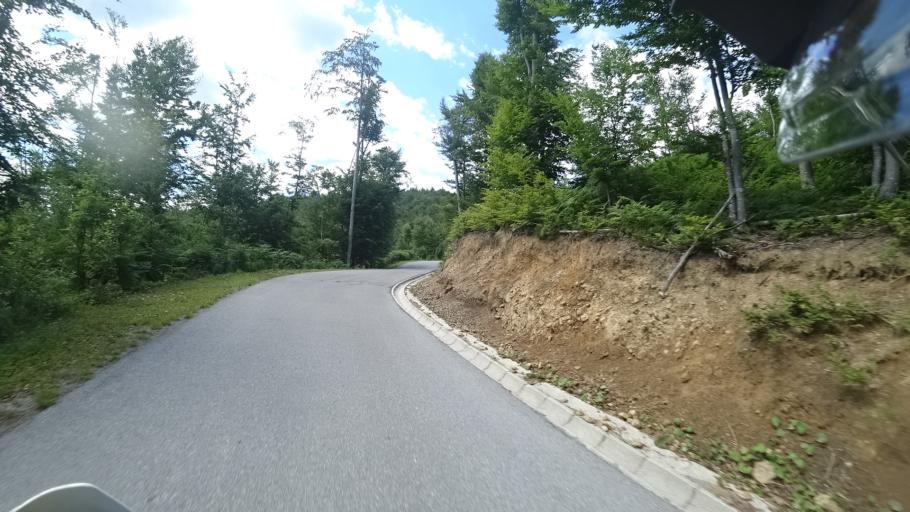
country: SI
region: Osilnica
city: Osilnica
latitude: 45.5140
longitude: 14.6624
